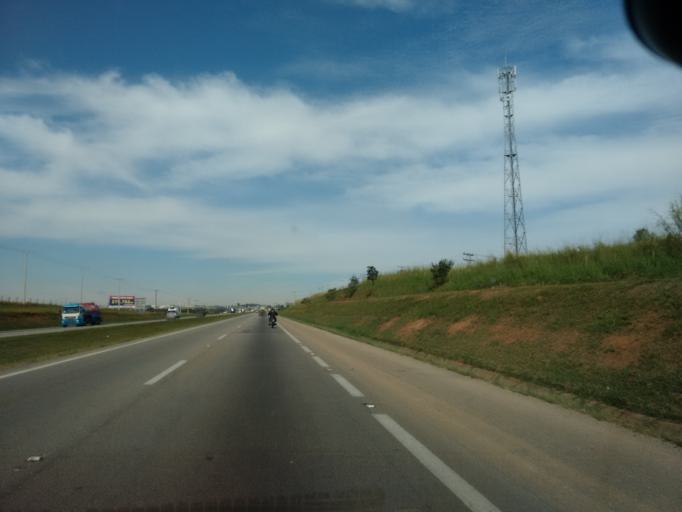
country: BR
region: Sao Paulo
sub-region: Itu
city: Itu
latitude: -23.2855
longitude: -47.3291
